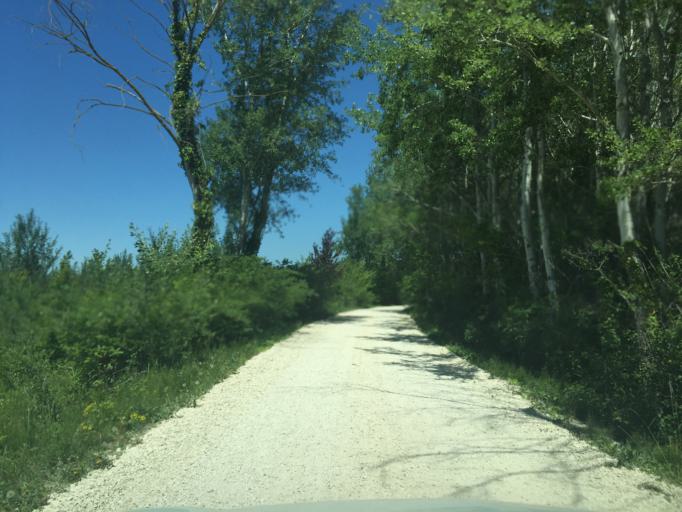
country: FR
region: Languedoc-Roussillon
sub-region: Departement du Gard
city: Roquemaure
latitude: 44.0576
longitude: 4.7945
